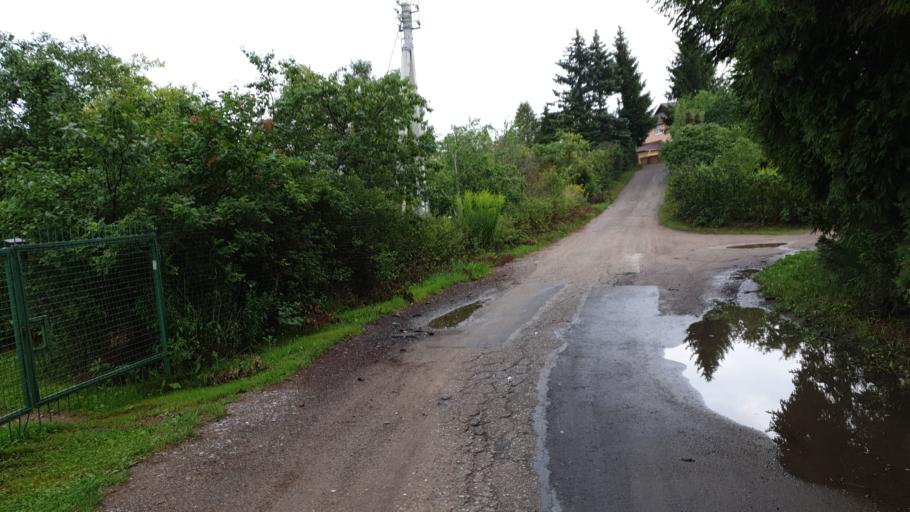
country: LT
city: Grigiskes
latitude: 54.7670
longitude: 25.0166
